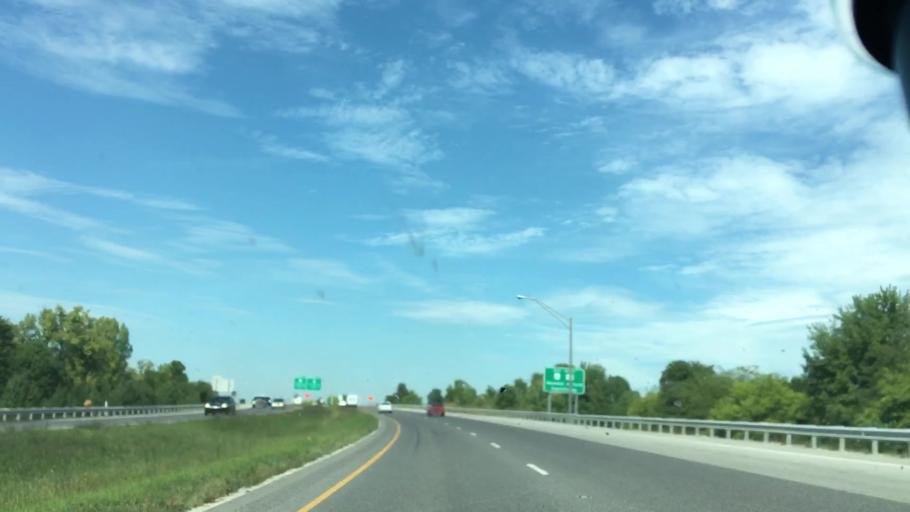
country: US
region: Kentucky
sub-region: Daviess County
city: Owensboro
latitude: 37.7431
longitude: -87.0716
